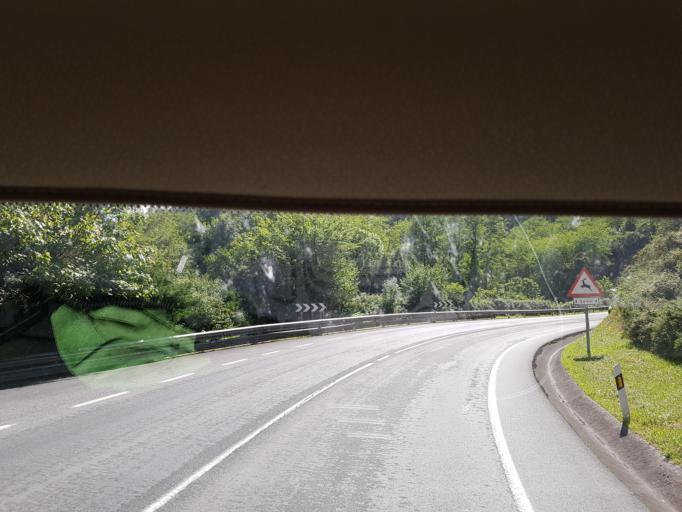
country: ES
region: Basque Country
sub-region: Bizkaia
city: San Julian de Muskiz
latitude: 43.3111
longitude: -3.1203
